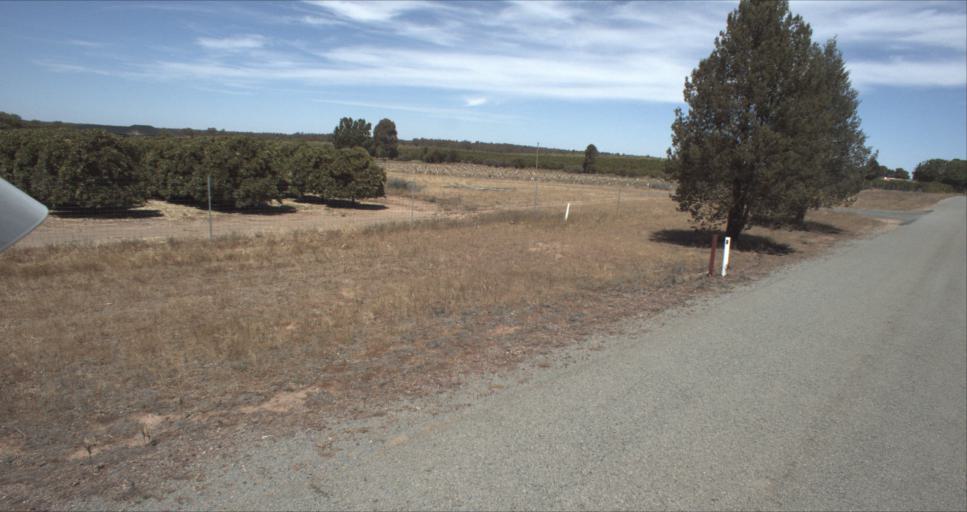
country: AU
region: New South Wales
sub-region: Leeton
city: Leeton
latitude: -34.6741
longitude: 146.4439
